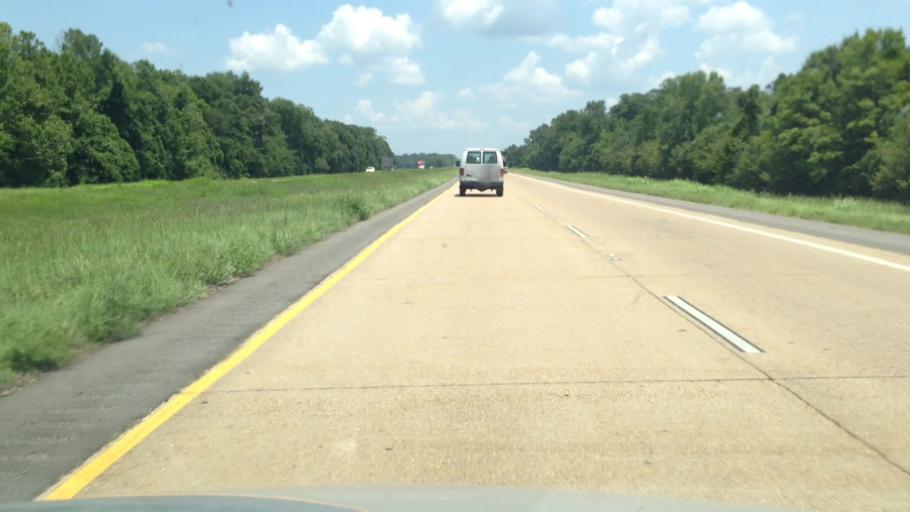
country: US
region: Louisiana
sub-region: Rapides Parish
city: Lecompte
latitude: 31.0076
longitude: -92.3586
